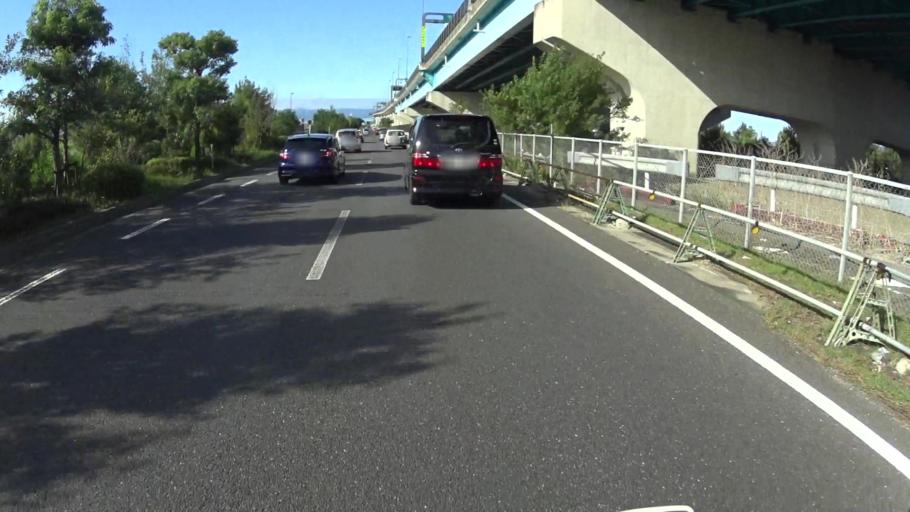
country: JP
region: Kyoto
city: Uji
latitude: 34.9011
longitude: 135.7499
